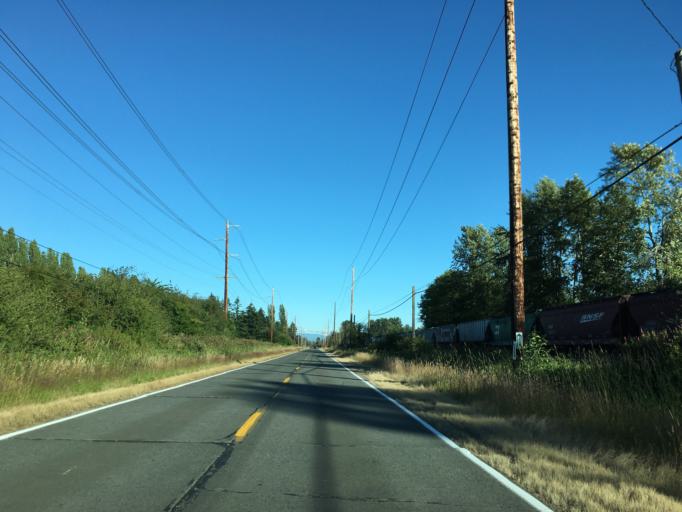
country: US
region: Washington
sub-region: Whatcom County
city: Birch Bay
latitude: 48.9267
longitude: -122.6546
